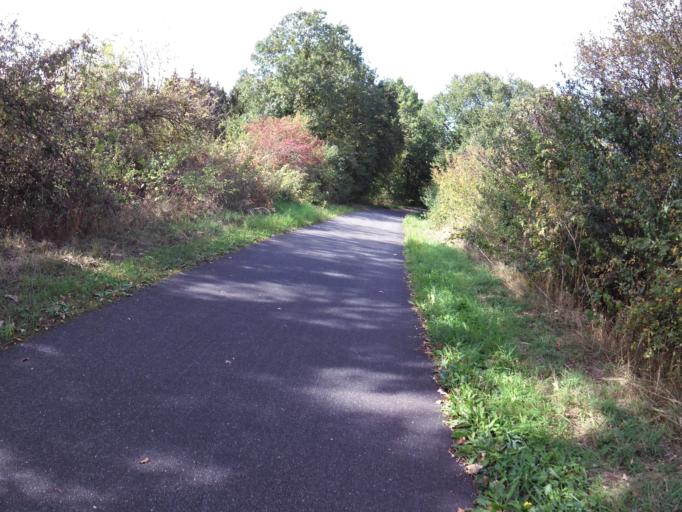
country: DE
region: Rheinland-Pfalz
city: Bleialf
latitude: 50.2203
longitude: 6.2692
